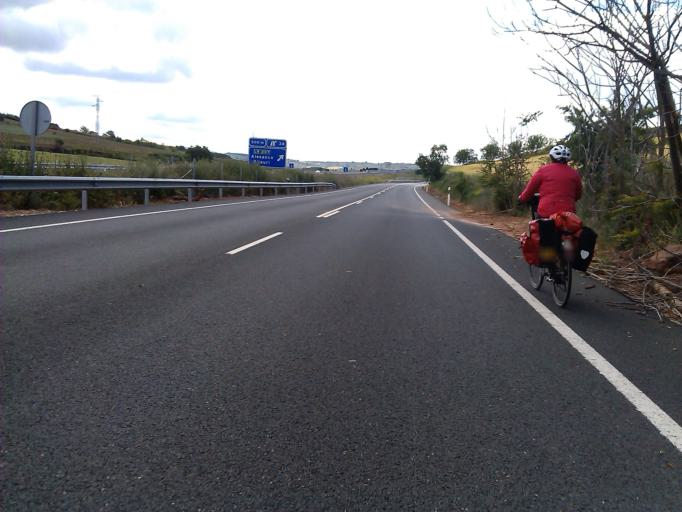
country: ES
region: La Rioja
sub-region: Provincia de La Rioja
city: Alesanco
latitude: 42.4343
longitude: -2.8227
